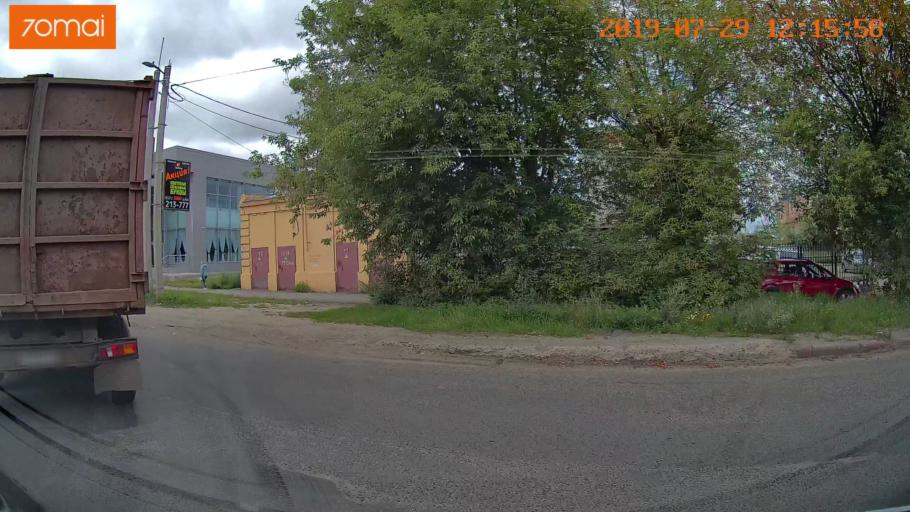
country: RU
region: Ivanovo
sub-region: Gorod Ivanovo
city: Ivanovo
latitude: 57.0106
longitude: 40.9543
